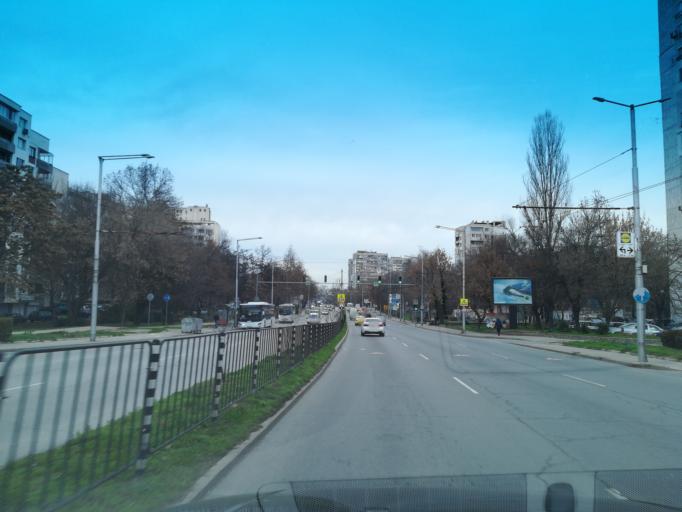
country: BG
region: Plovdiv
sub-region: Obshtina Plovdiv
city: Plovdiv
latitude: 42.1556
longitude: 24.7312
